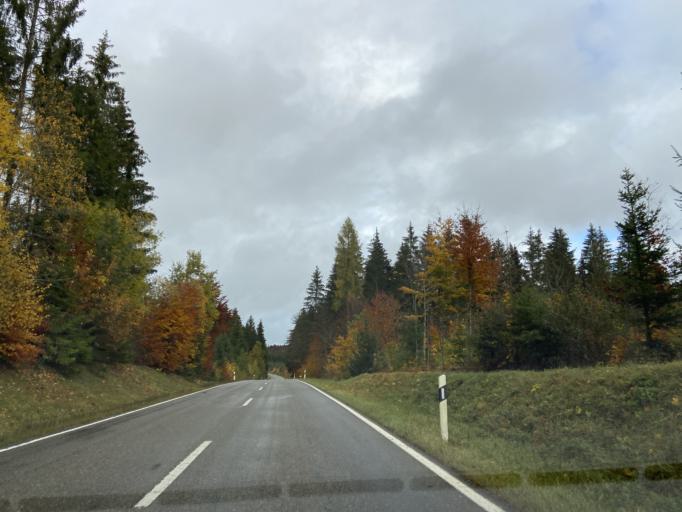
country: DE
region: Baden-Wuerttemberg
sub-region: Tuebingen Region
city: Beuron
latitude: 48.0499
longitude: 8.9538
